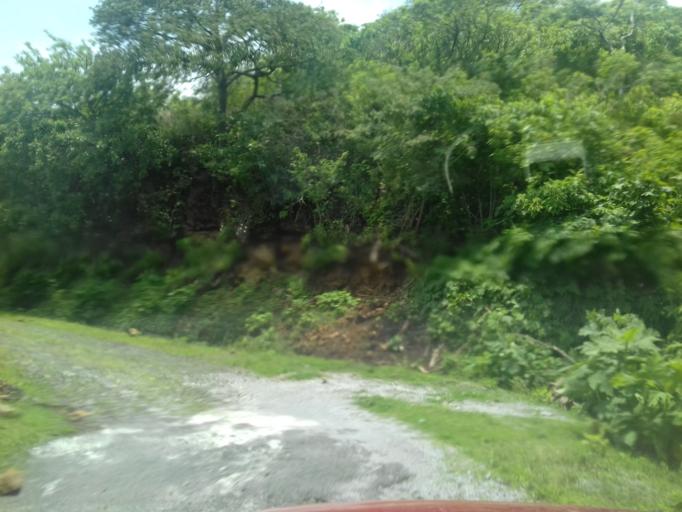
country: MX
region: Nayarit
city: Jala
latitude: 21.1092
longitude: -104.4887
